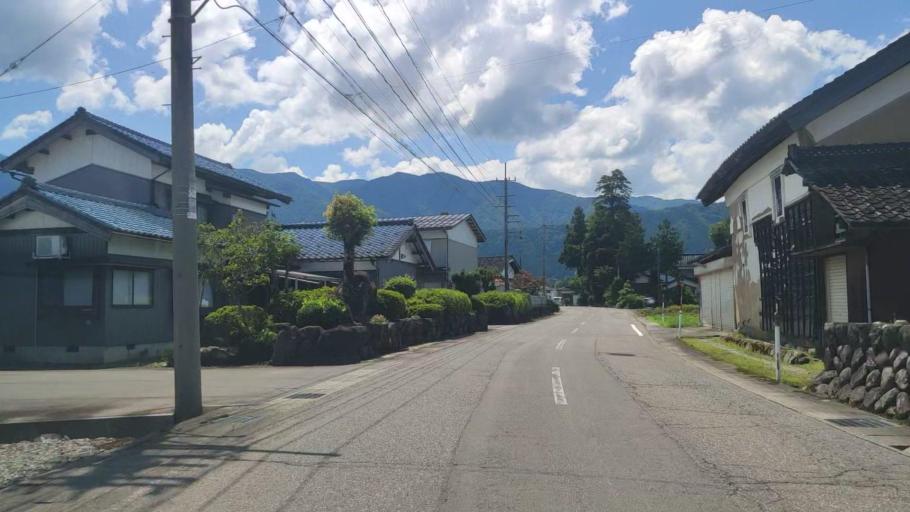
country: JP
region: Fukui
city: Ono
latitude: 35.9496
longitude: 136.5407
